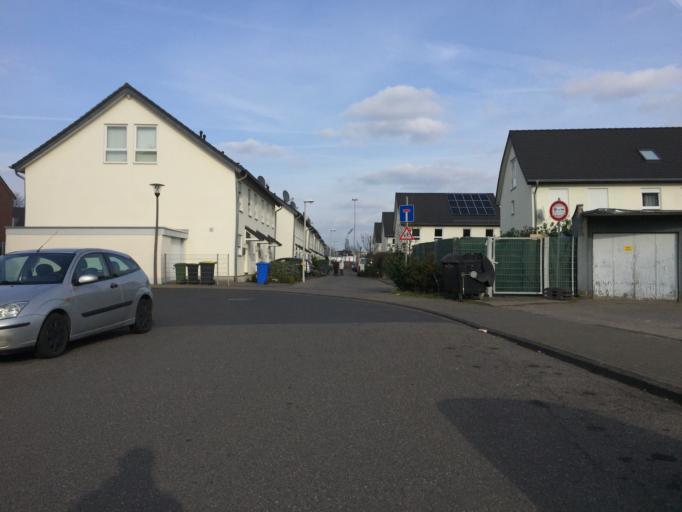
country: DE
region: North Rhine-Westphalia
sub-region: Regierungsbezirk Koln
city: Bonn
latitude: 50.7456
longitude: 7.0782
